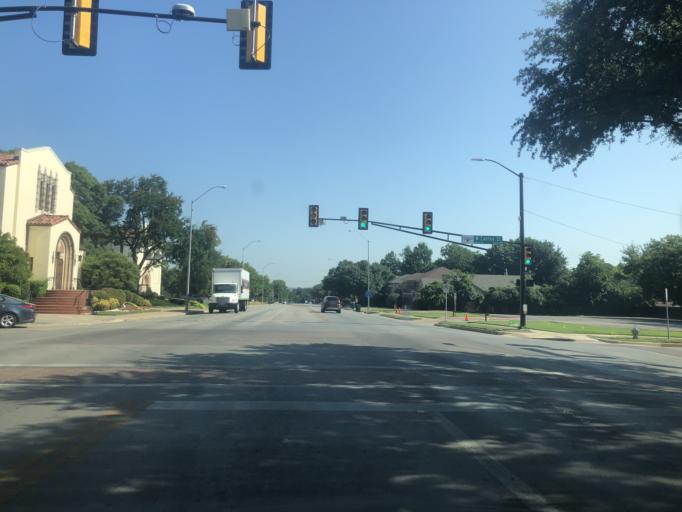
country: US
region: Texas
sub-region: Tarrant County
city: Fort Worth
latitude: 32.7115
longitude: -97.3604
